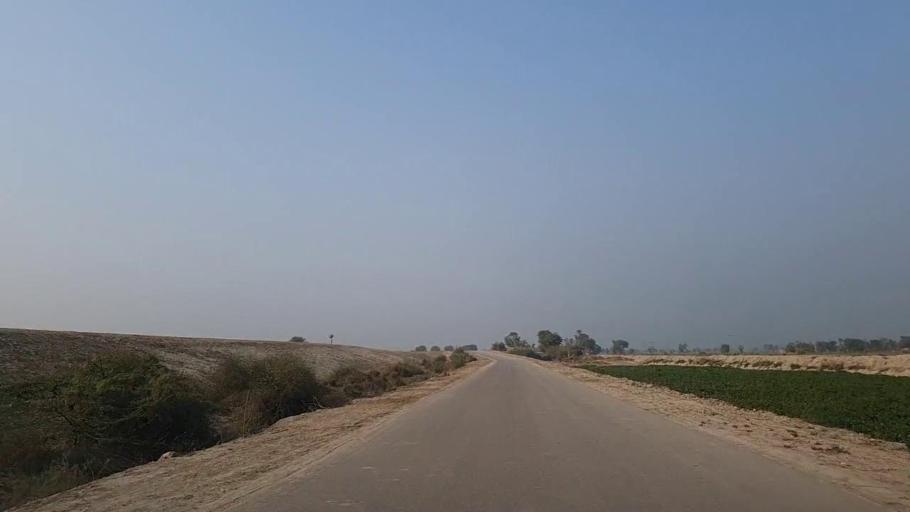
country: PK
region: Sindh
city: Sann
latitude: 26.1169
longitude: 68.1501
